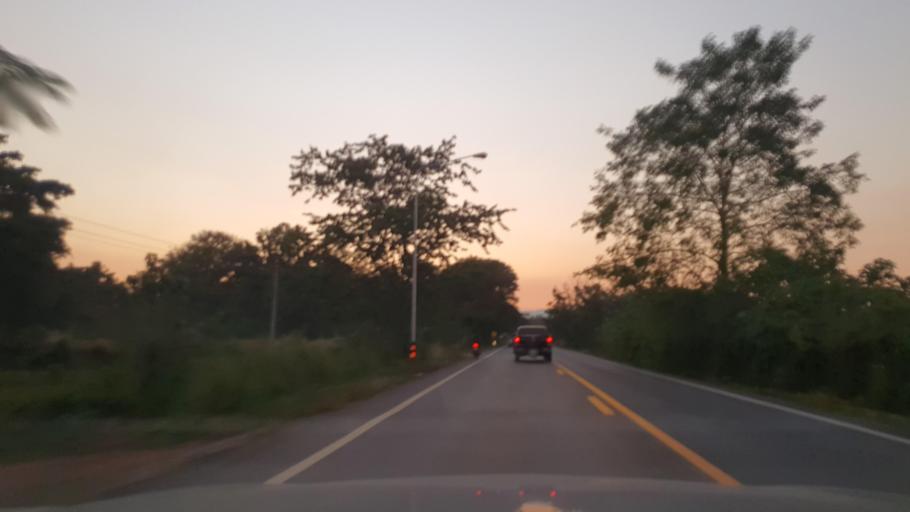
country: TH
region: Phayao
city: Dok Kham Tai
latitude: 19.1482
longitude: 100.0112
